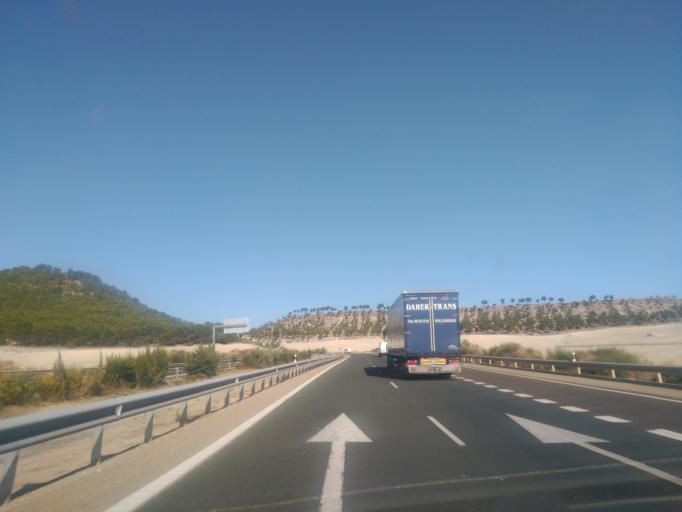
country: ES
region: Castille and Leon
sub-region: Provincia de Valladolid
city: Cisterniga
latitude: 41.6039
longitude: -4.6632
